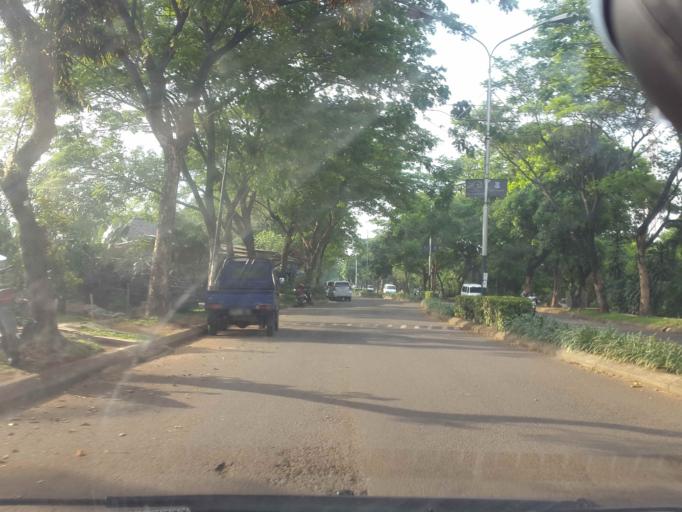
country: ID
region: Banten
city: South Tangerang
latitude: -6.2720
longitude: 106.6916
